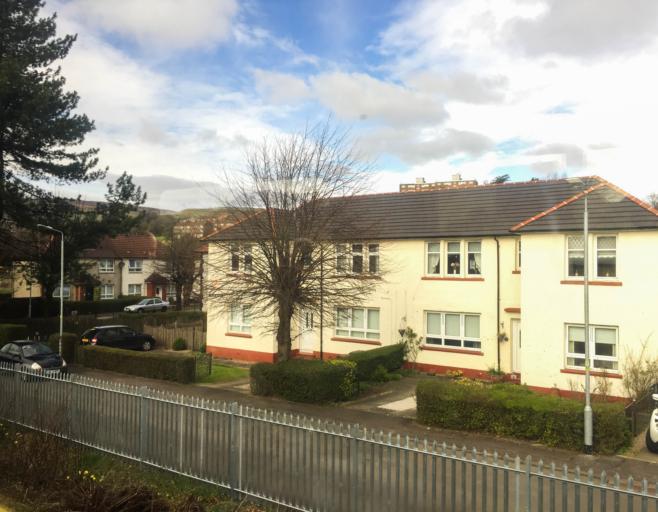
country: GB
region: Scotland
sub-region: West Dunbartonshire
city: Old Kilpatrick
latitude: 55.9158
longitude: -4.4360
